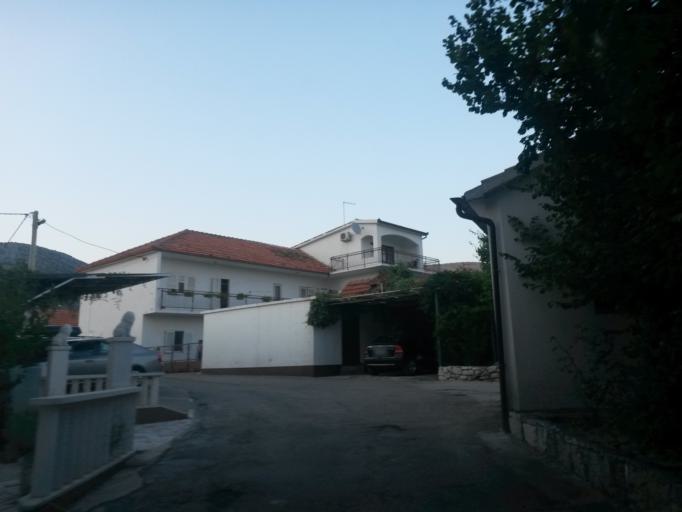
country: HR
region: Splitsko-Dalmatinska
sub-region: Grad Trogir
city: Trogir
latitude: 43.5129
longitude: 16.1837
